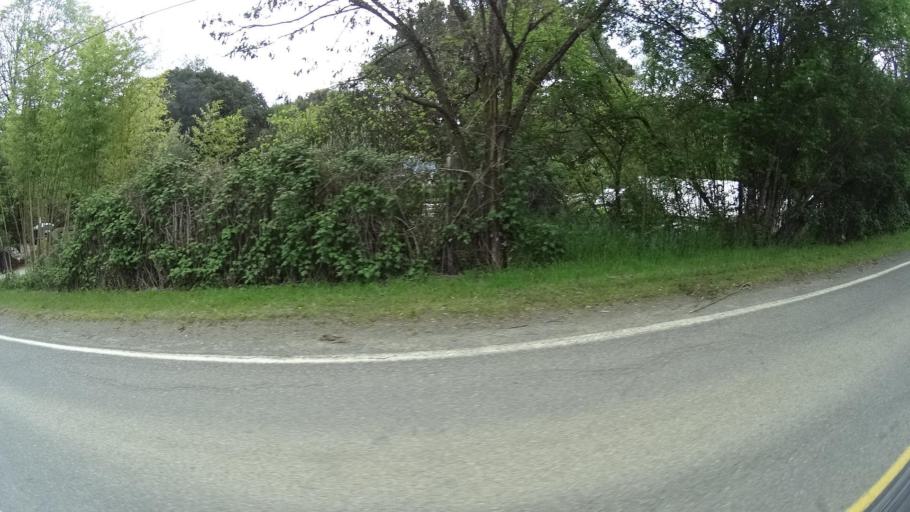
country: US
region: California
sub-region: Humboldt County
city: Redway
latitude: 40.1087
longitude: -123.8990
